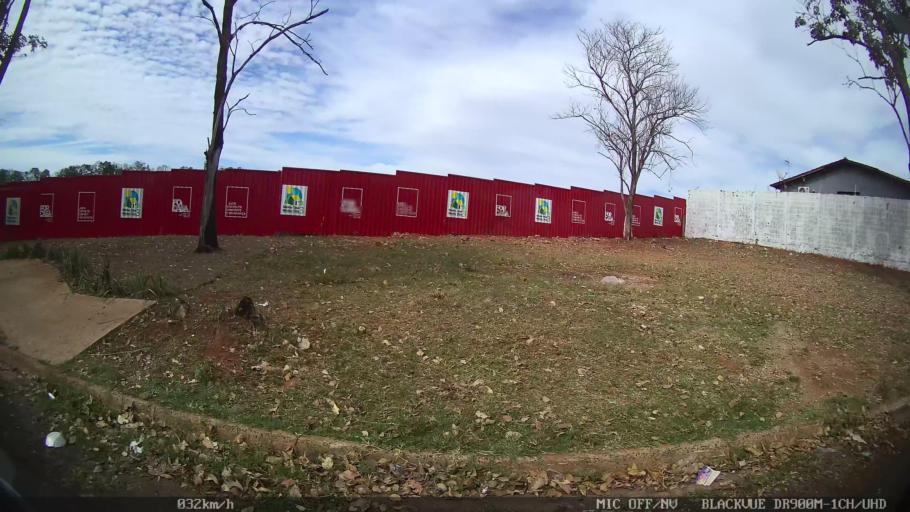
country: BR
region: Sao Paulo
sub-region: Catanduva
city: Catanduva
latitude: -21.1562
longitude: -48.9732
